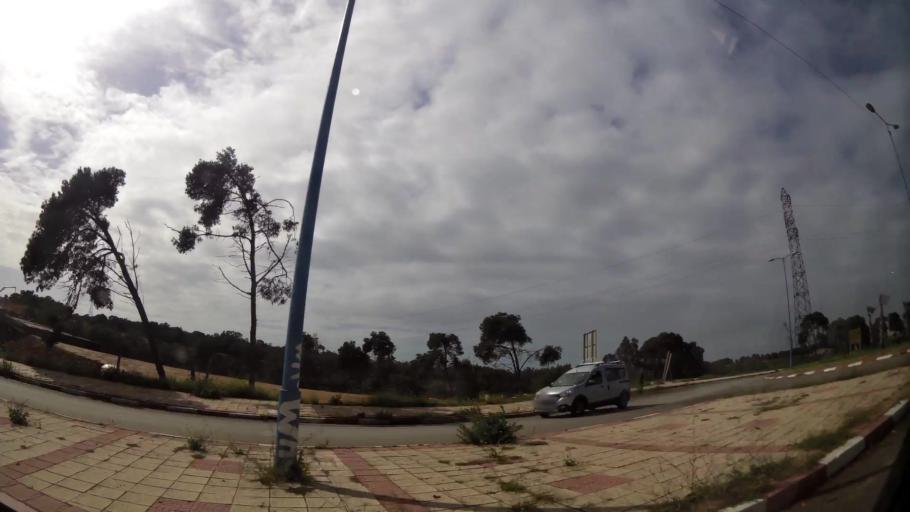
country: MA
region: Grand Casablanca
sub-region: Mohammedia
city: Mohammedia
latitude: 33.6672
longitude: -7.3987
